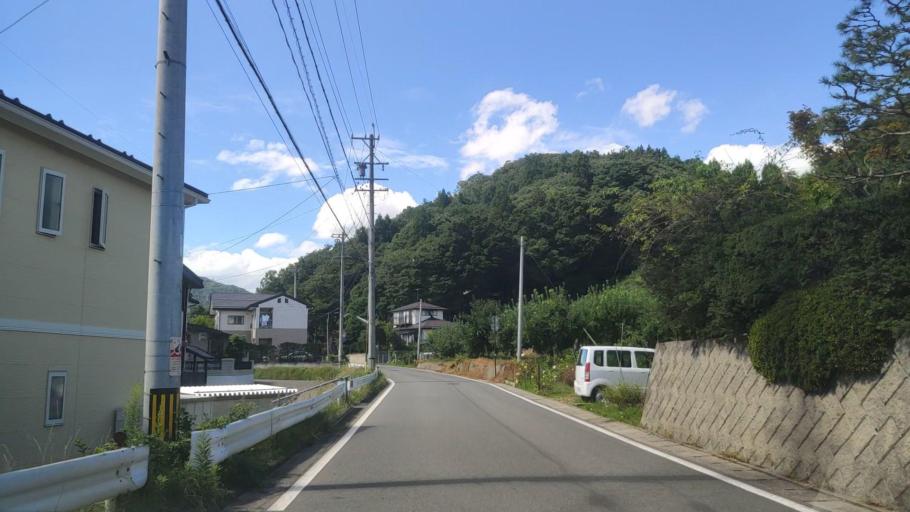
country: JP
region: Nagano
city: Nagano-shi
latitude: 36.6881
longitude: 138.2146
